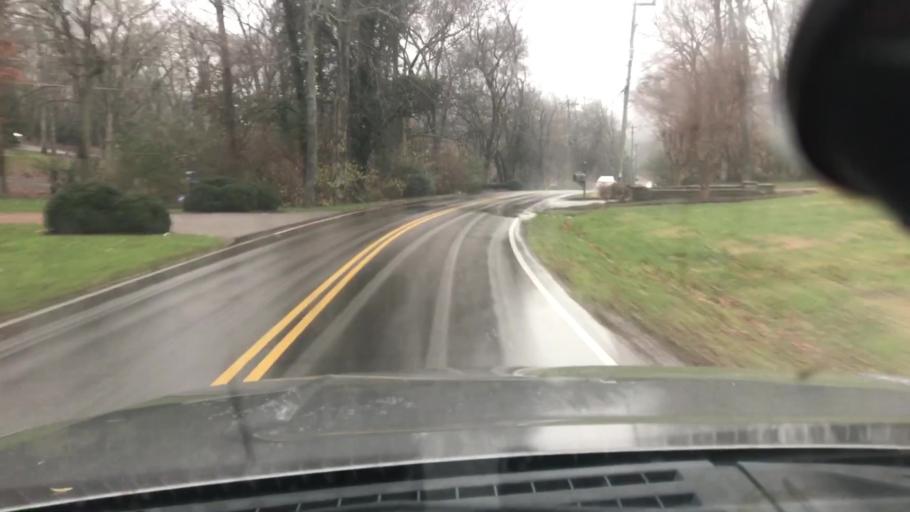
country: US
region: Tennessee
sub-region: Davidson County
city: Forest Hills
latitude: 36.0722
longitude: -86.8616
